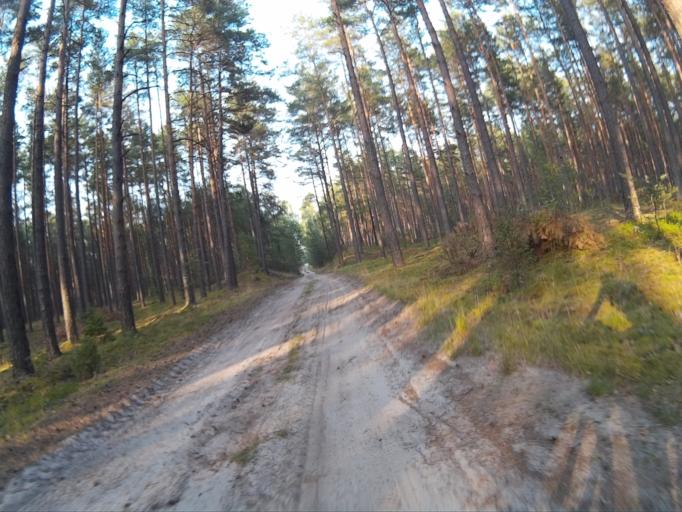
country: PL
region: Pomeranian Voivodeship
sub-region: Powiat chojnicki
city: Czersk
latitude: 53.6967
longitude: 17.9640
